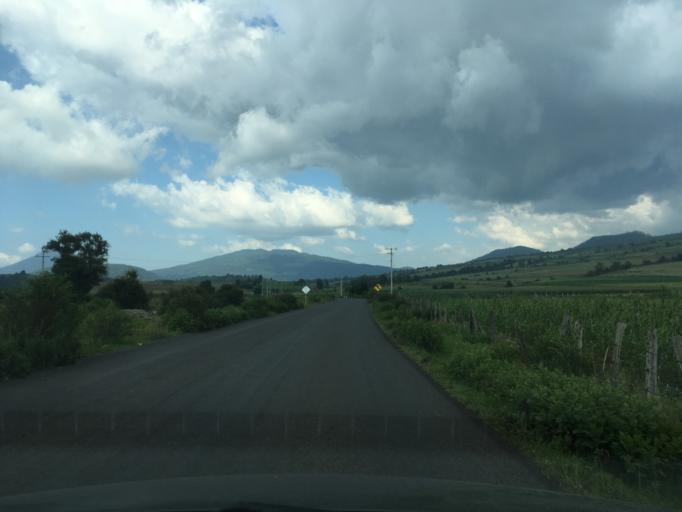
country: MX
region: Michoacan
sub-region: Nahuatzen
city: Sevina
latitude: 19.6040
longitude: -101.9484
